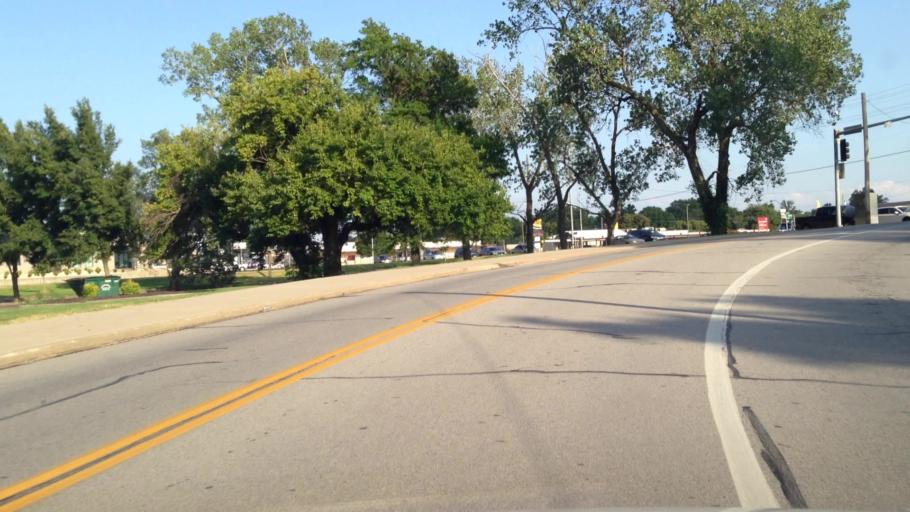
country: US
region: Missouri
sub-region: Jasper County
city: Joplin
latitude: 37.0845
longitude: -94.5029
